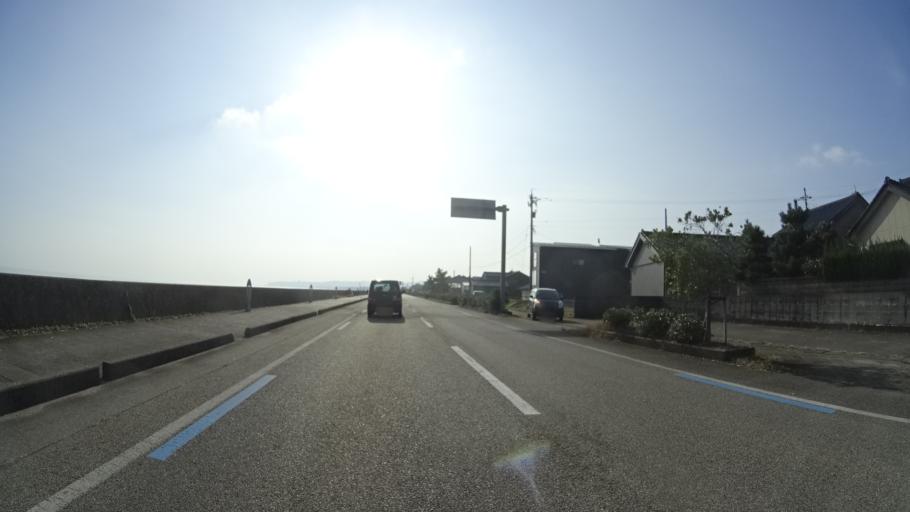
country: JP
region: Toyama
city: Himi
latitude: 36.8542
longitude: 136.9906
